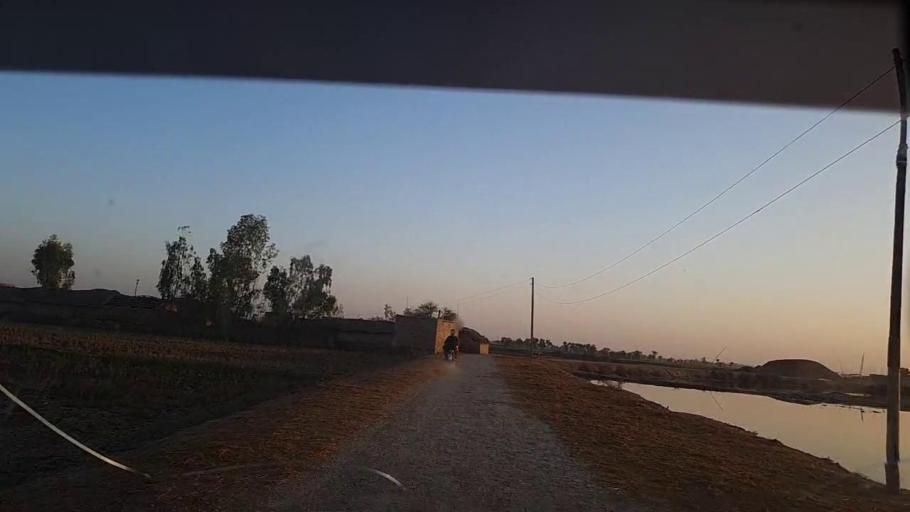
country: PK
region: Sindh
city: Ratodero
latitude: 27.8905
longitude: 68.2363
